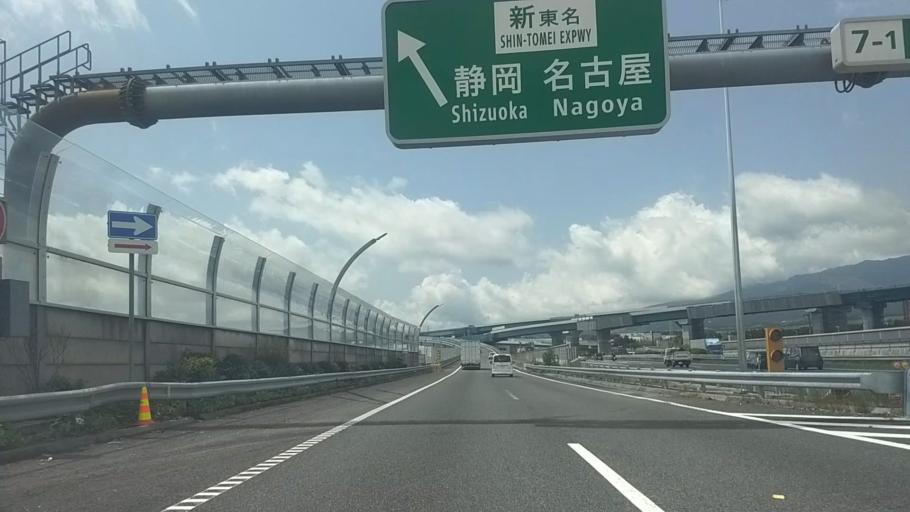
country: JP
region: Shizuoka
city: Gotemba
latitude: 35.2674
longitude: 138.9143
